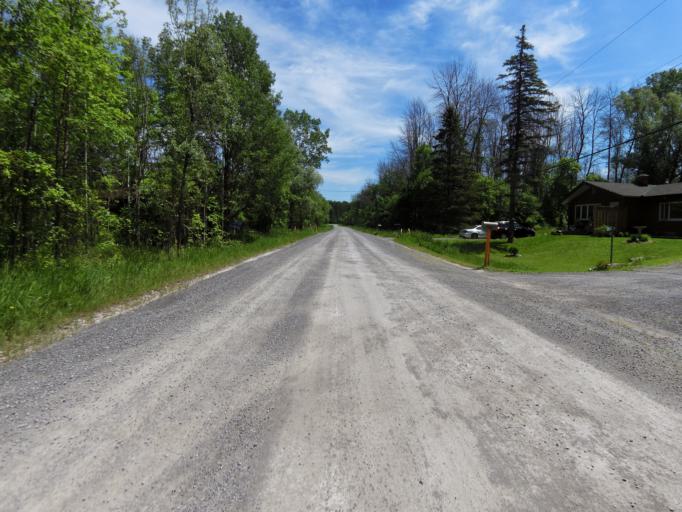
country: CA
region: Ontario
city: Ottawa
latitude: 45.3441
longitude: -75.6114
